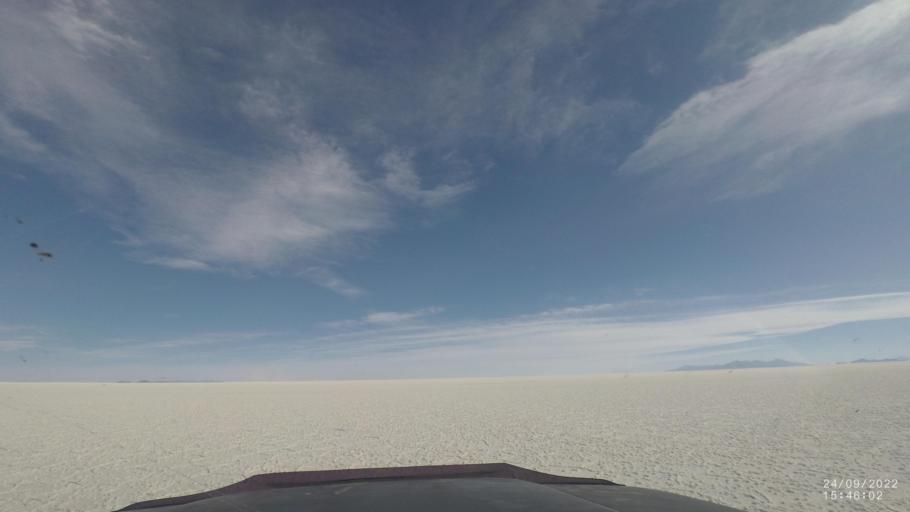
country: BO
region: Potosi
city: Colchani
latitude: -20.2626
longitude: -67.2216
